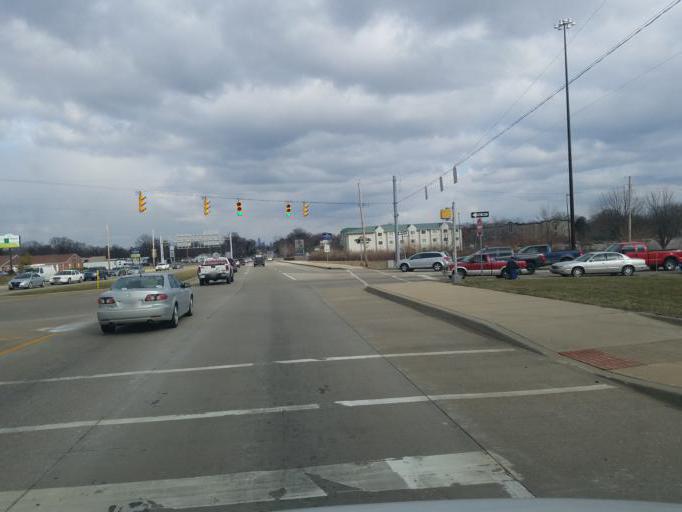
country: US
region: Indiana
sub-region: Marion County
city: Speedway
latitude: 39.7648
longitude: -86.2648
